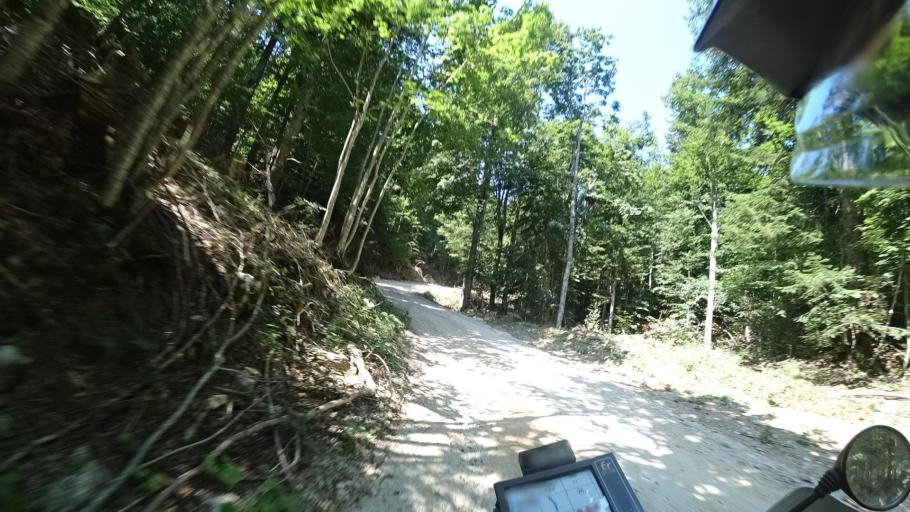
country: HR
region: Licko-Senjska
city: Popovaca
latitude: 44.5713
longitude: 15.2045
